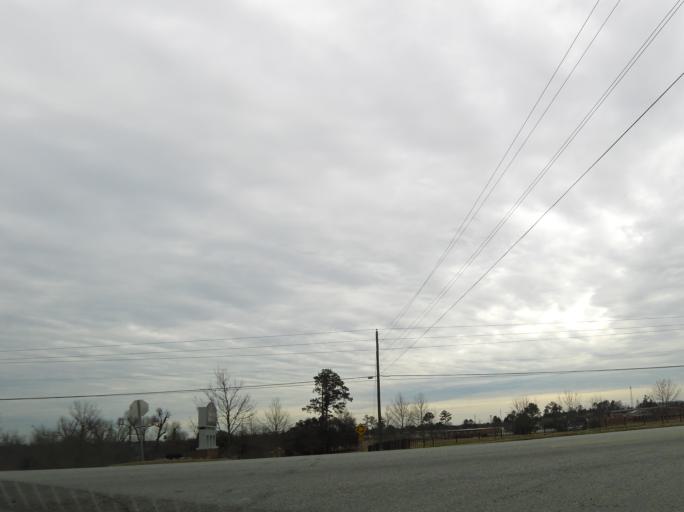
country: US
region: Georgia
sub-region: Bibb County
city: West Point
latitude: 32.8152
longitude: -83.7334
